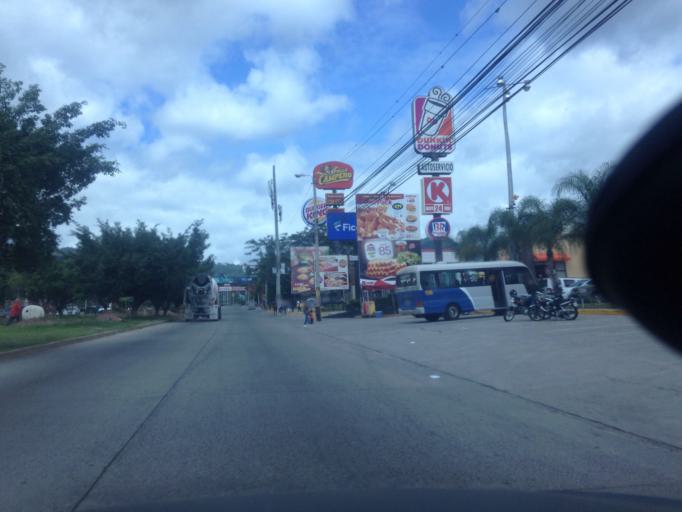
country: HN
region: Francisco Morazan
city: Tegucigalpa
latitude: 14.0833
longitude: -87.1673
